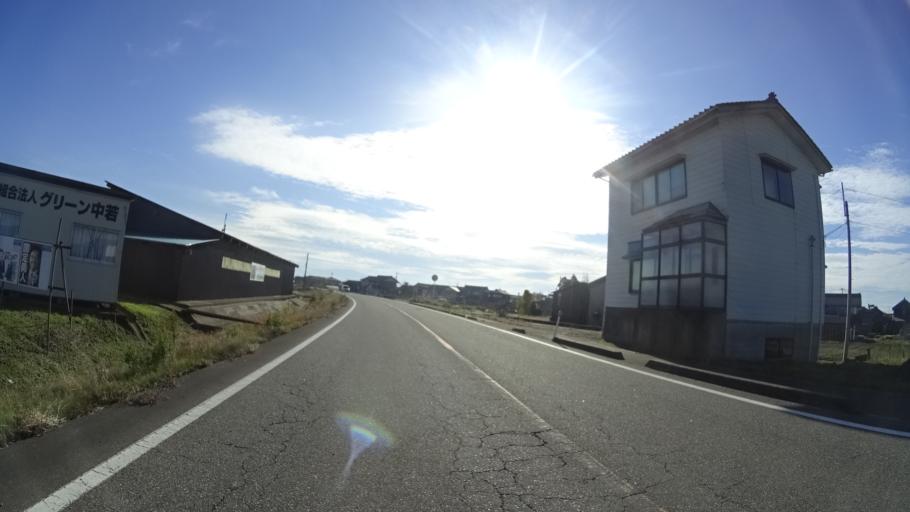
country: JP
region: Niigata
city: Mitsuke
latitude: 37.5764
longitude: 138.8362
